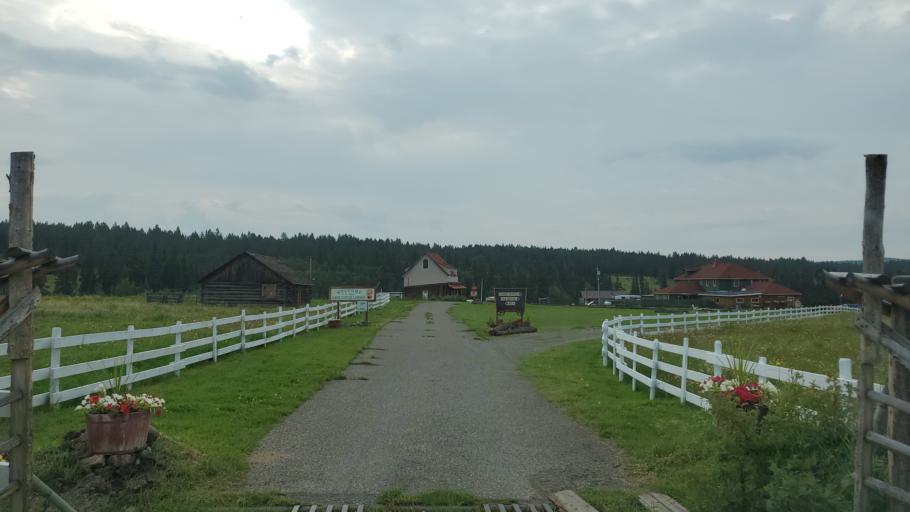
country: CA
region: British Columbia
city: Williams Lake
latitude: 51.9693
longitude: -122.5302
